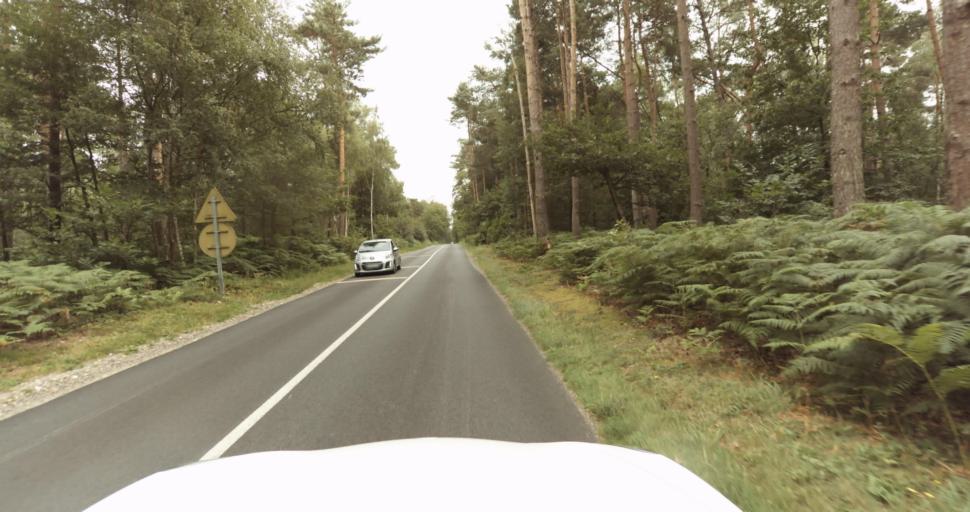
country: FR
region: Haute-Normandie
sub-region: Departement de l'Eure
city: Saint-Sebastien-de-Morsent
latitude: 48.9879
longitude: 1.0582
